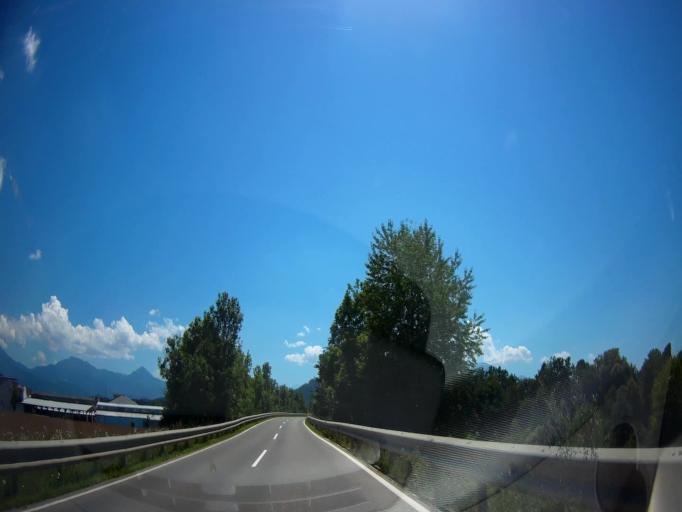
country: AT
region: Carinthia
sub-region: Politischer Bezirk Volkermarkt
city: Eberndorf
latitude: 46.6233
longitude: 14.6154
